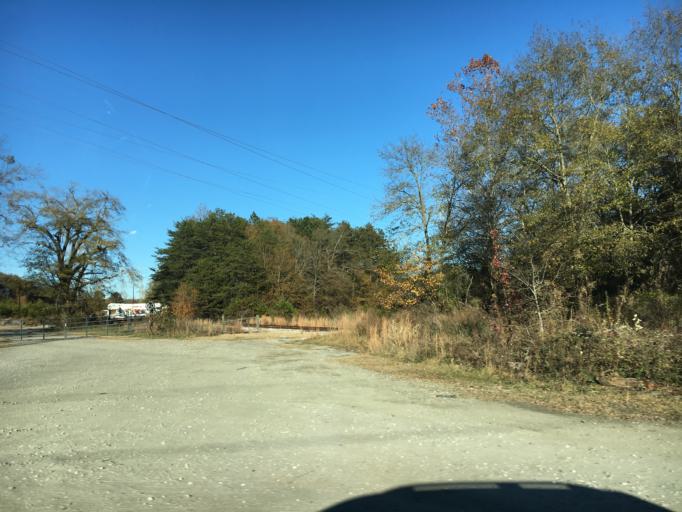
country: US
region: South Carolina
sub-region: Spartanburg County
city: Duncan
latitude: 34.9488
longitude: -82.1587
